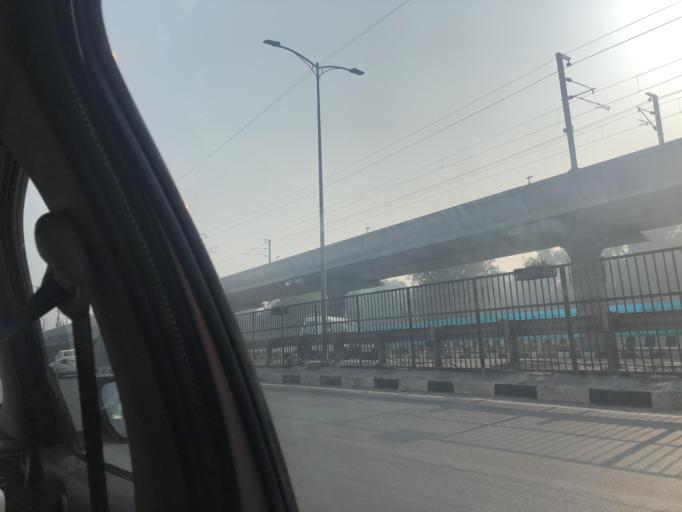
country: IN
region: NCT
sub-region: Central Delhi
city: Karol Bagh
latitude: 28.5879
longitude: 77.1507
